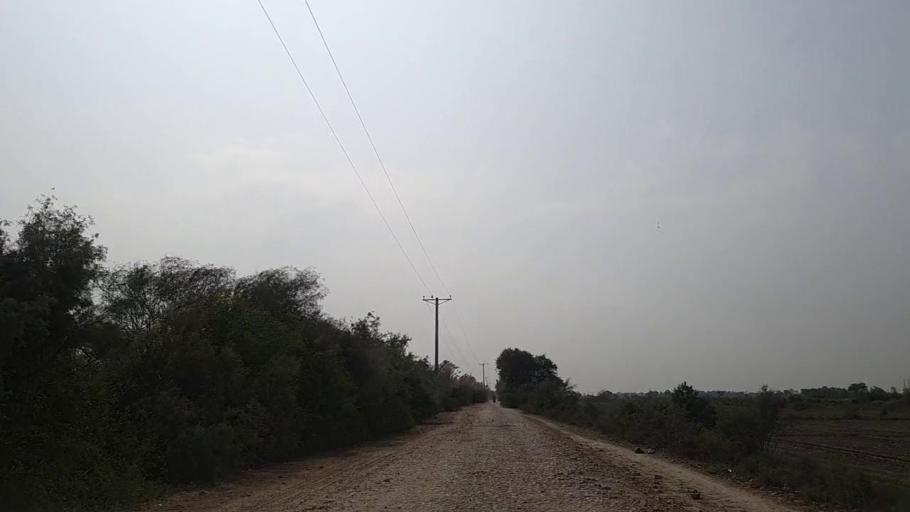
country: PK
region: Sindh
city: Mirpur Sakro
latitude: 24.6312
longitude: 67.7468
